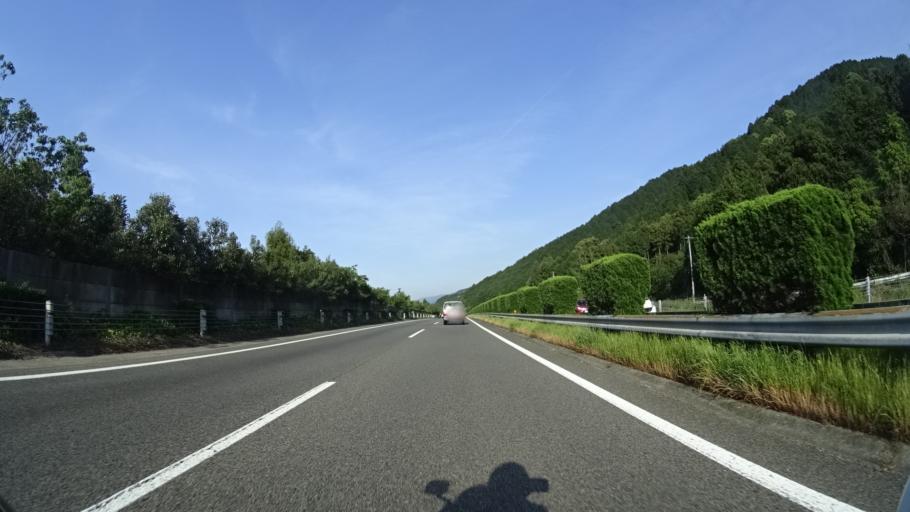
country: JP
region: Ehime
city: Niihama
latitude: 33.9524
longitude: 133.4428
